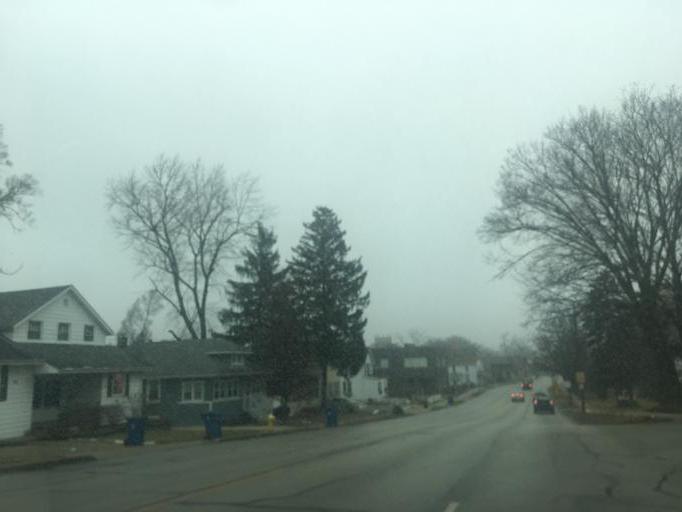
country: US
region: Illinois
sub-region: DuPage County
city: Downers Grove
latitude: 41.7893
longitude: -88.0095
